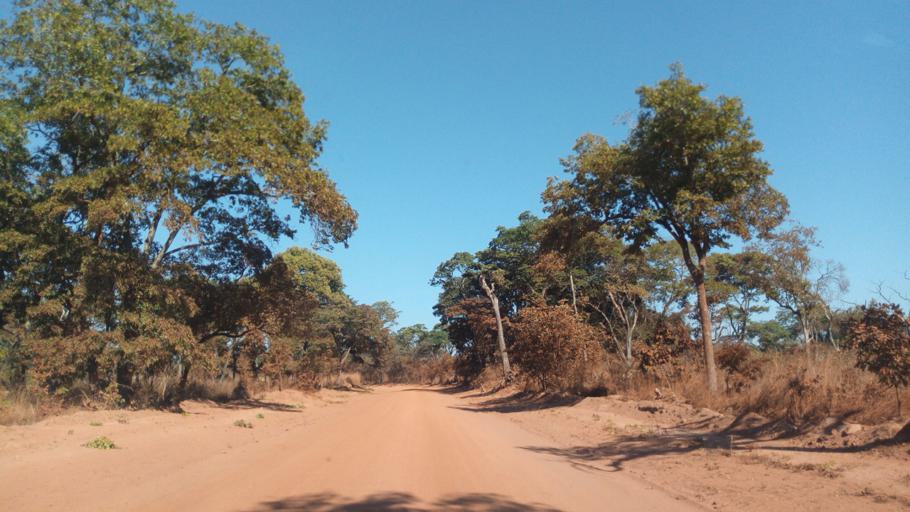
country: ZM
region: Luapula
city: Mwense
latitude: -10.7331
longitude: 28.3454
